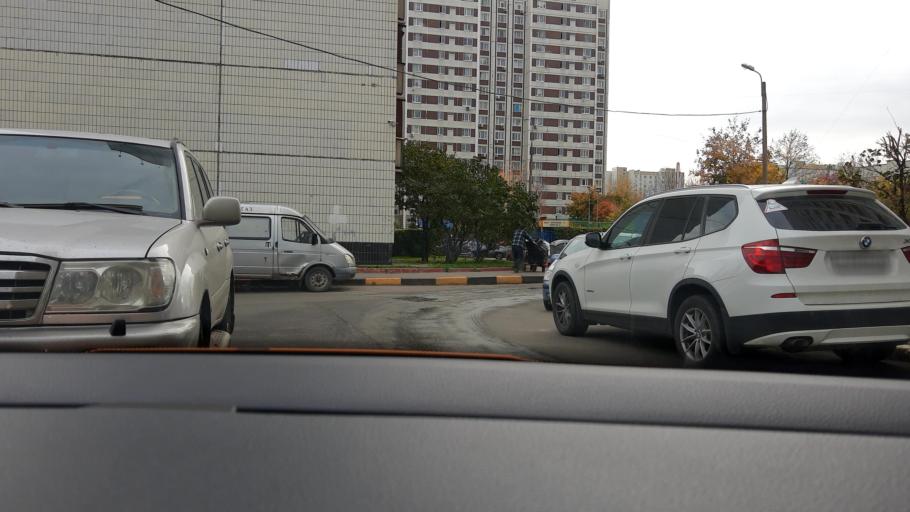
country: RU
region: Moscow
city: Orekhovo-Borisovo
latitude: 55.6353
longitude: 37.7382
